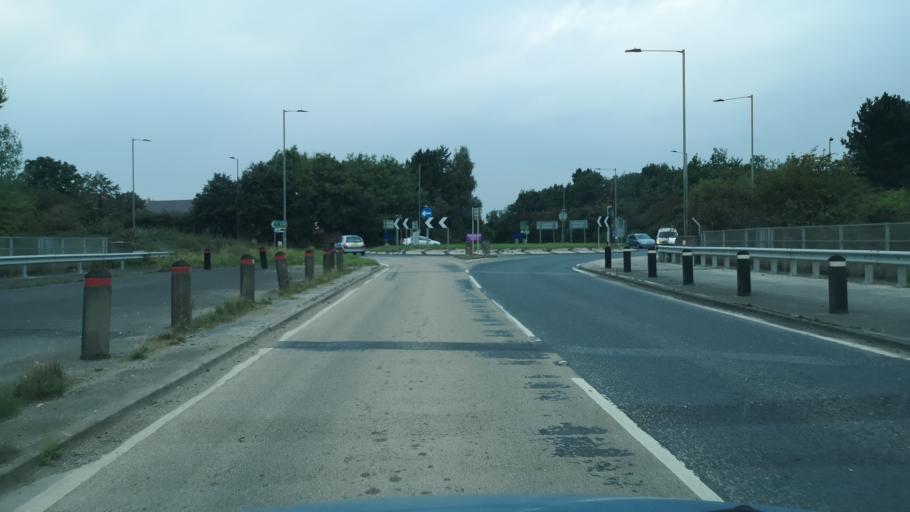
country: GB
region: England
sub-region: North Yorkshire
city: Hambleton
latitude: 53.7043
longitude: -1.1426
